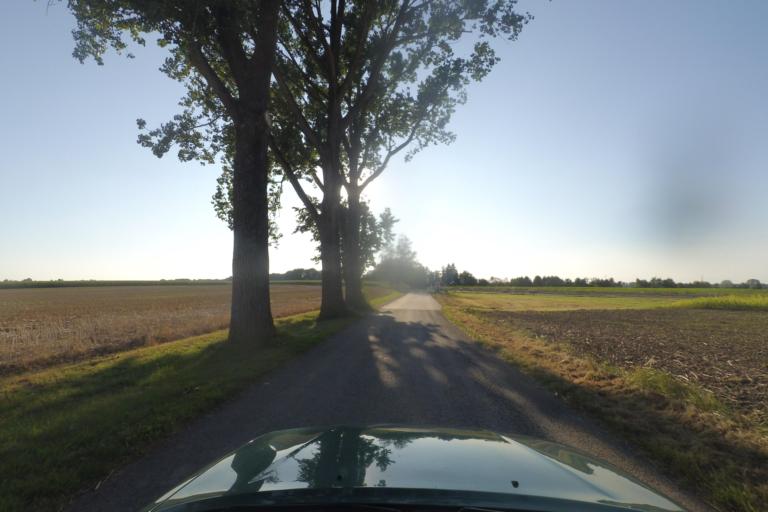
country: DE
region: Bavaria
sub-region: Swabia
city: Brunnen
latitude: 48.2447
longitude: 10.9621
